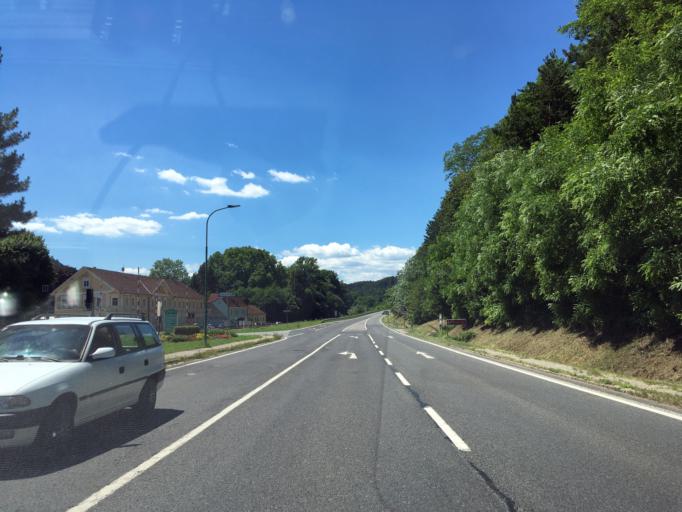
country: AT
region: Lower Austria
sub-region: Politischer Bezirk Neunkirchen
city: Seebenstein
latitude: 47.7030
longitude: 16.1424
